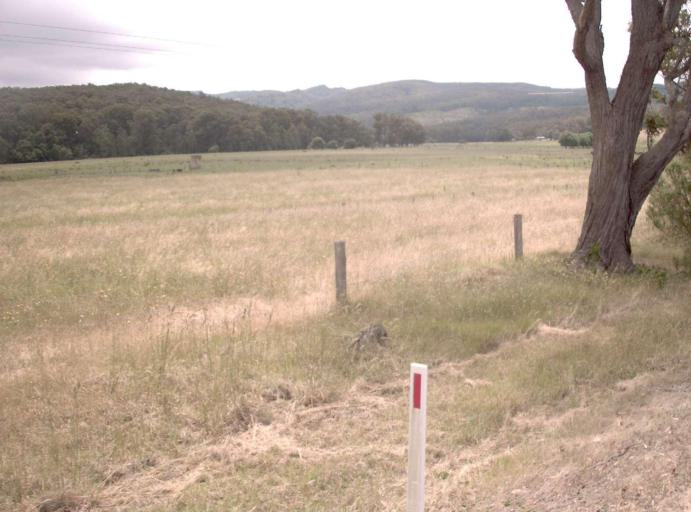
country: AU
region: Victoria
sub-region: Latrobe
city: Traralgon
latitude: -38.4821
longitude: 146.6815
